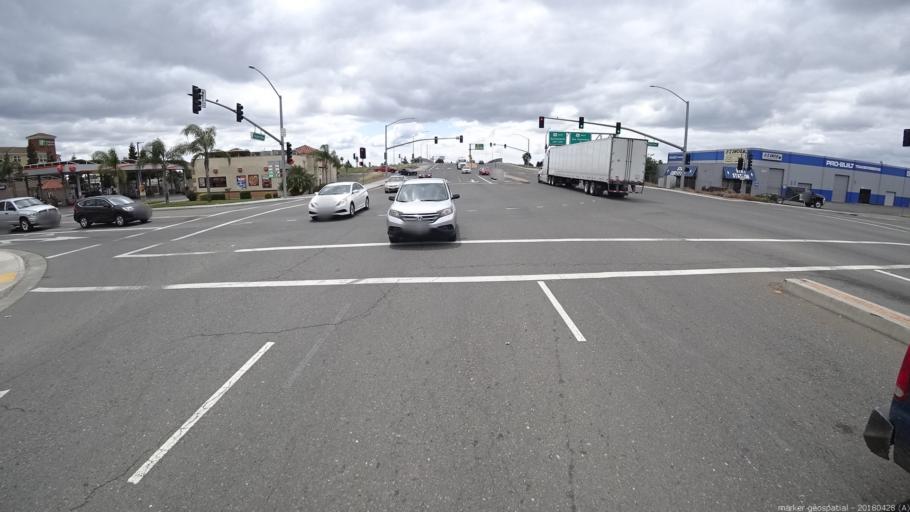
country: US
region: California
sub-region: Yolo County
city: West Sacramento
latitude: 38.5770
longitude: -121.5486
